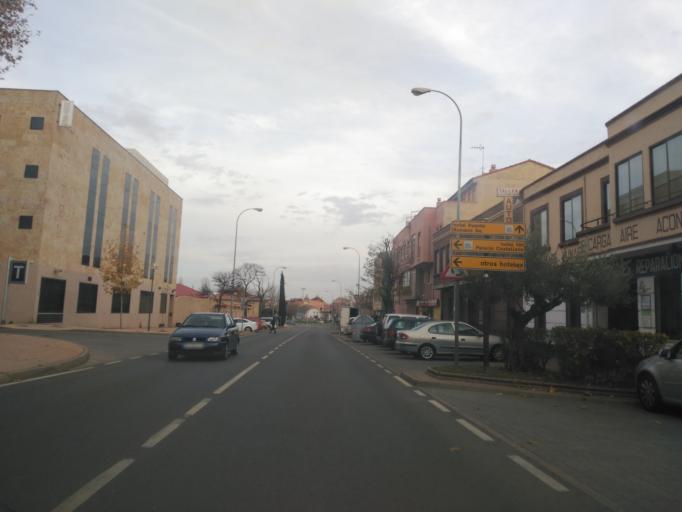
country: ES
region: Castille and Leon
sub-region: Provincia de Salamanca
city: Salamanca
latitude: 40.9550
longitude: -5.6788
